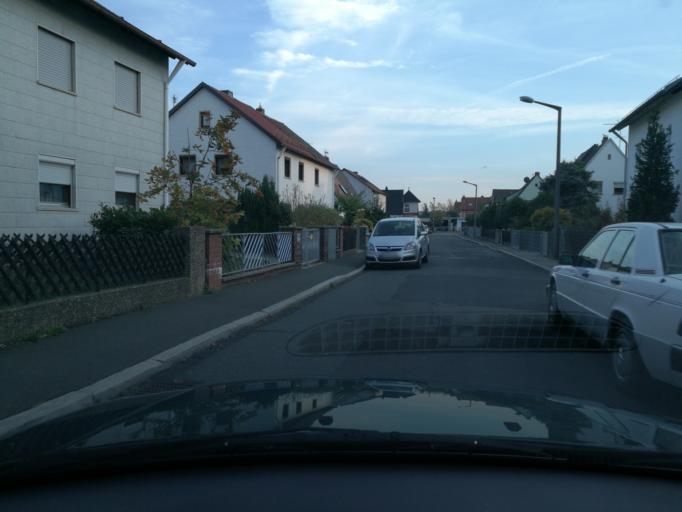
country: DE
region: Bavaria
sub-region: Regierungsbezirk Mittelfranken
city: Obermichelbach
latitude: 49.4909
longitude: 10.9352
